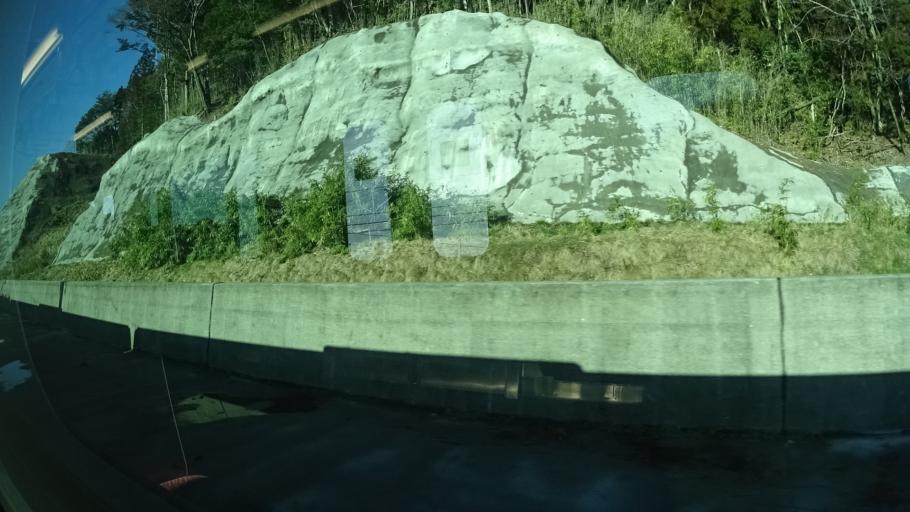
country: JP
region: Fukushima
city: Namie
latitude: 37.4589
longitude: 141.0091
